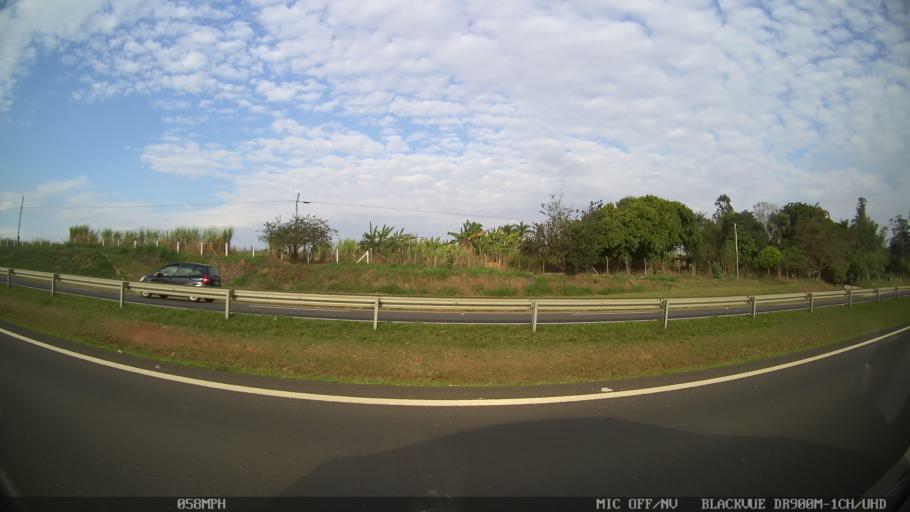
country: BR
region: Sao Paulo
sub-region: Cosmopolis
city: Cosmopolis
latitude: -22.6144
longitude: -47.1965
